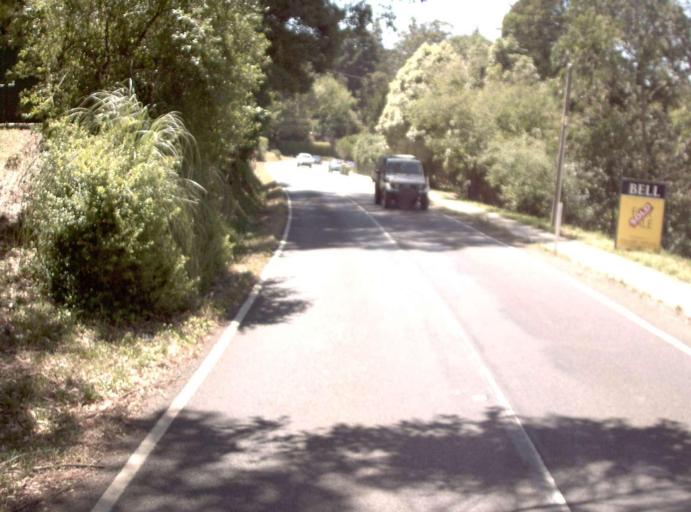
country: AU
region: Victoria
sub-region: Yarra Ranges
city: Kalorama
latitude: -37.8224
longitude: 145.3647
